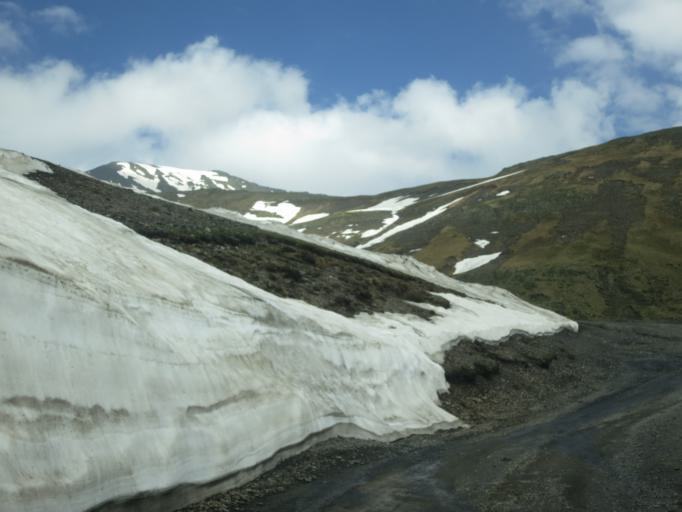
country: GE
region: Kakheti
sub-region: Telavi
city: Telavi
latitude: 42.2836
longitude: 45.5024
